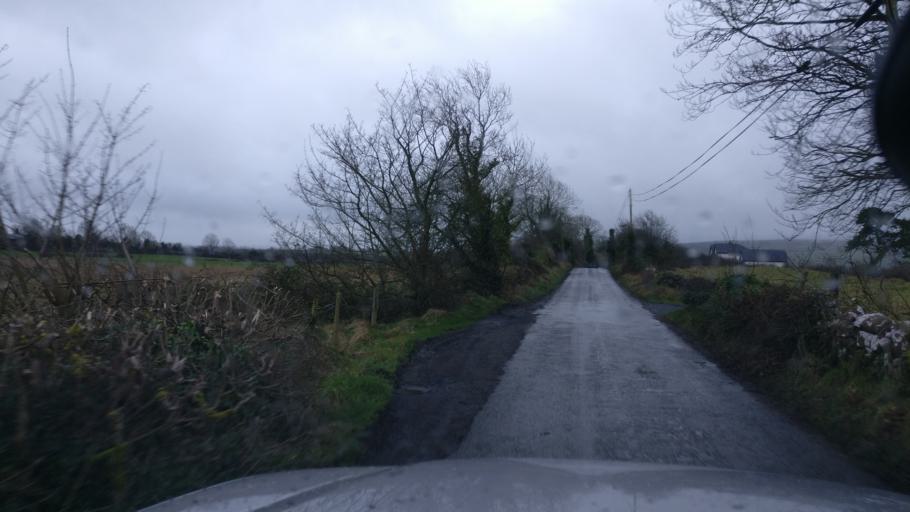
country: IE
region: Connaught
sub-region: County Galway
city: Loughrea
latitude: 53.1938
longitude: -8.6631
